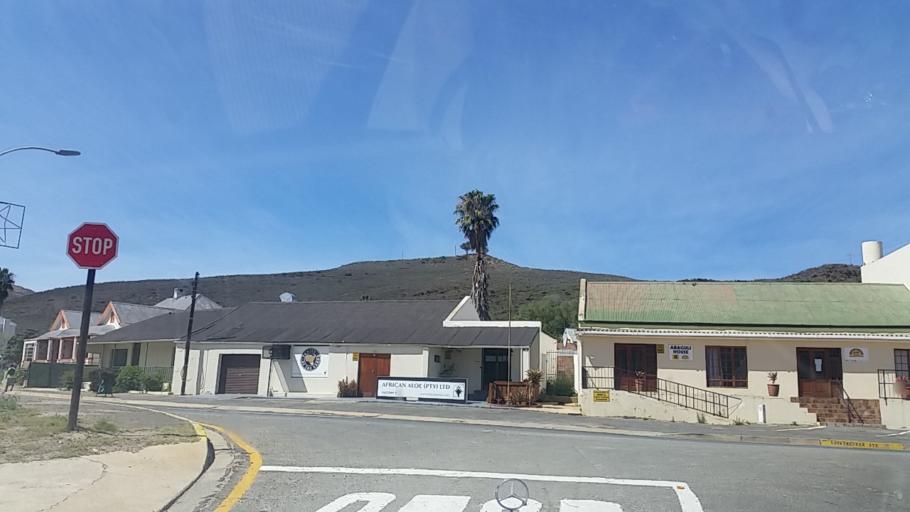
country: ZA
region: Western Cape
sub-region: Eden District Municipality
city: Knysna
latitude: -33.6545
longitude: 23.1304
